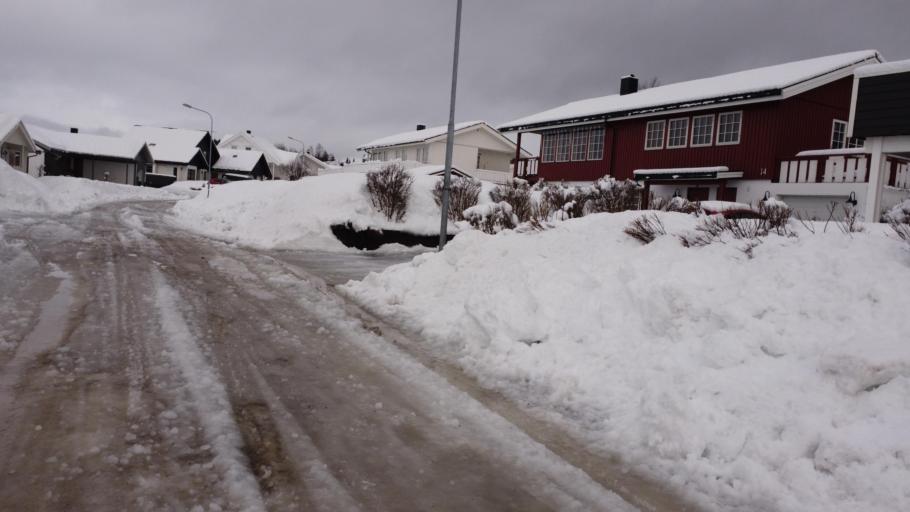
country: NO
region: Nordland
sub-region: Rana
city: Mo i Rana
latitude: 66.3318
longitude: 14.1524
